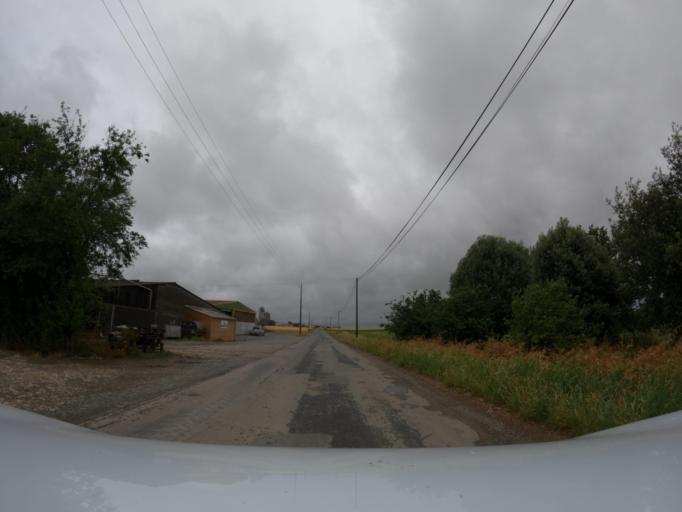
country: FR
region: Pays de la Loire
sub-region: Departement de la Vendee
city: Maillezais
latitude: 46.4045
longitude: -0.7268
